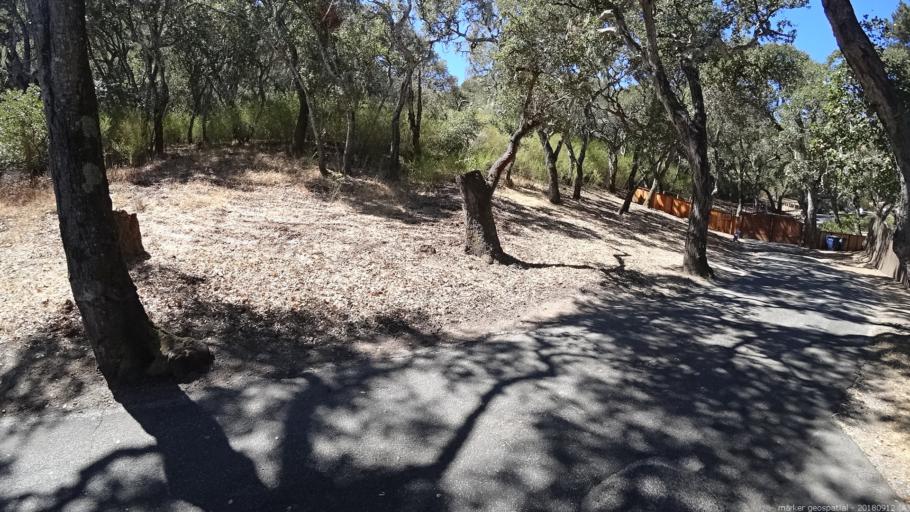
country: US
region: California
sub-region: Monterey County
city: Carmel Valley Village
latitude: 36.4678
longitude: -121.7321
